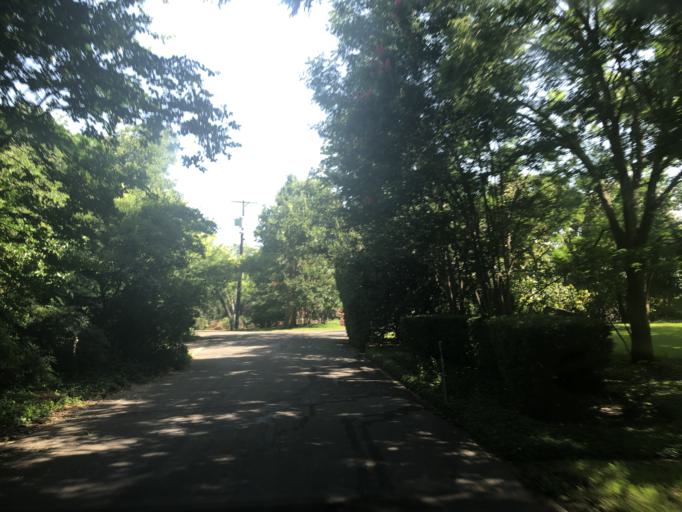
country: US
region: Texas
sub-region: Dallas County
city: University Park
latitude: 32.8808
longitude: -96.8168
